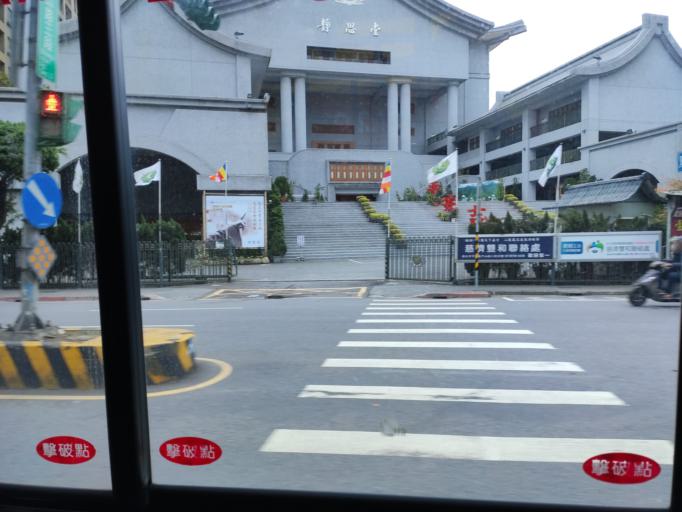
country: TW
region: Taipei
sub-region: Taipei
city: Banqiao
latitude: 25.0055
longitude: 121.4774
